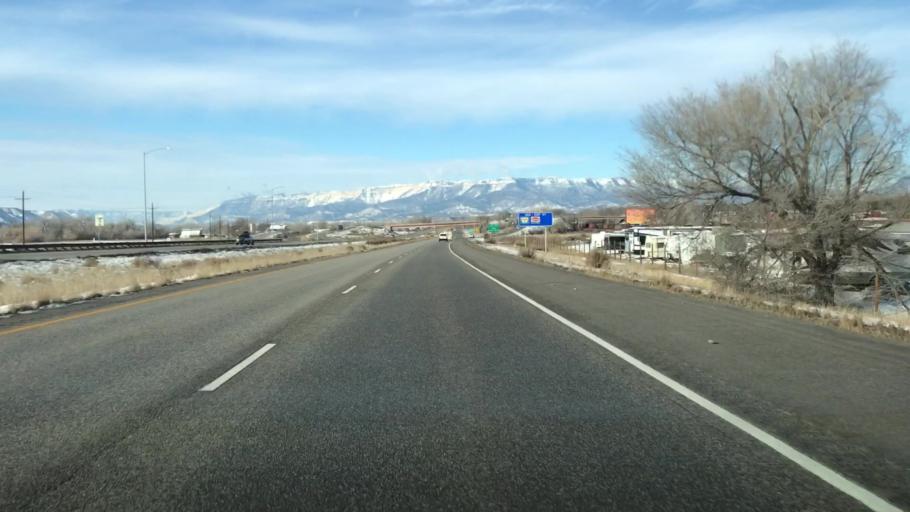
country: US
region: Colorado
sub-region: Garfield County
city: Silt
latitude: 39.5442
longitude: -107.6468
